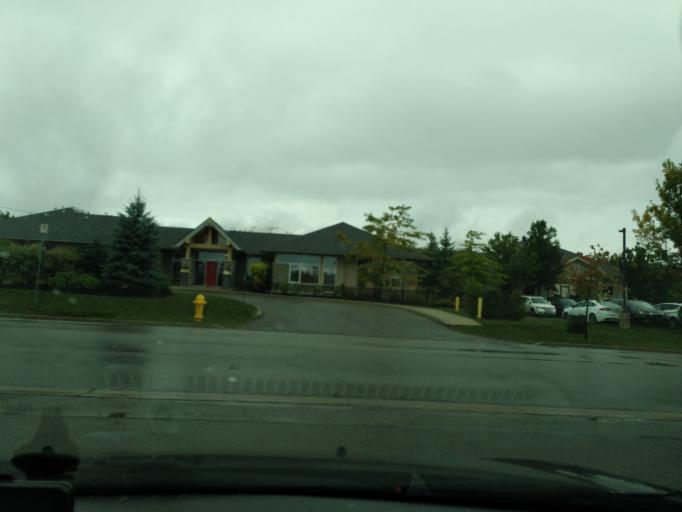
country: CA
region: Ontario
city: Barrie
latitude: 44.4154
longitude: -79.6577
